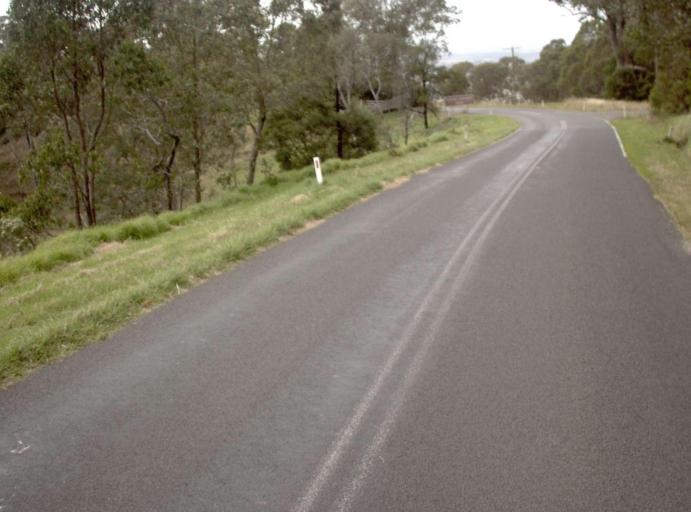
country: AU
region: Victoria
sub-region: Latrobe
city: Traralgon
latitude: -38.1348
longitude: 146.4764
